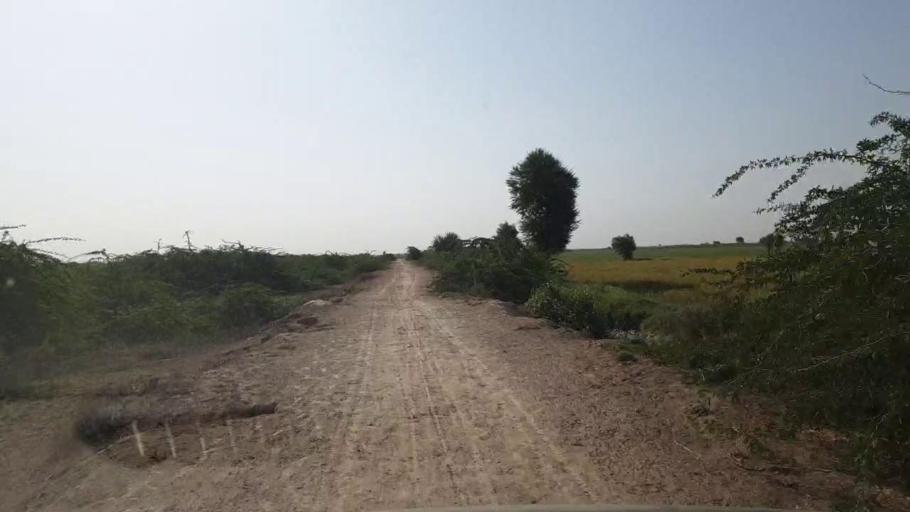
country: PK
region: Sindh
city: Kadhan
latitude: 24.5720
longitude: 69.0823
